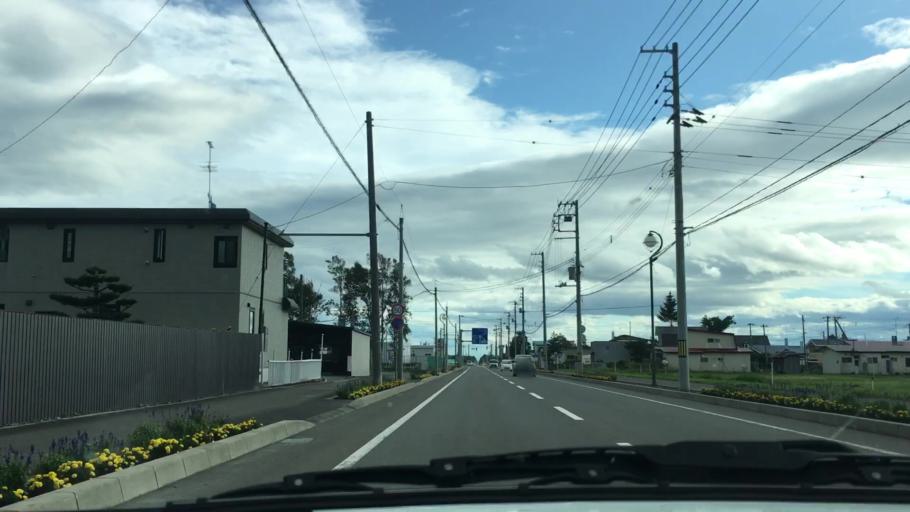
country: JP
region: Hokkaido
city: Otofuke
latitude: 43.2276
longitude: 143.2939
